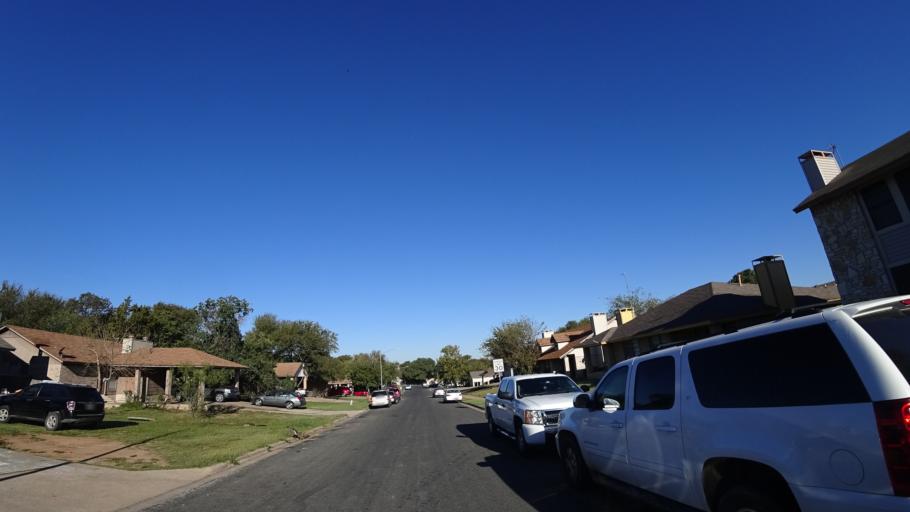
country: US
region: Texas
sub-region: Travis County
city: Hornsby Bend
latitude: 30.2217
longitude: -97.6666
